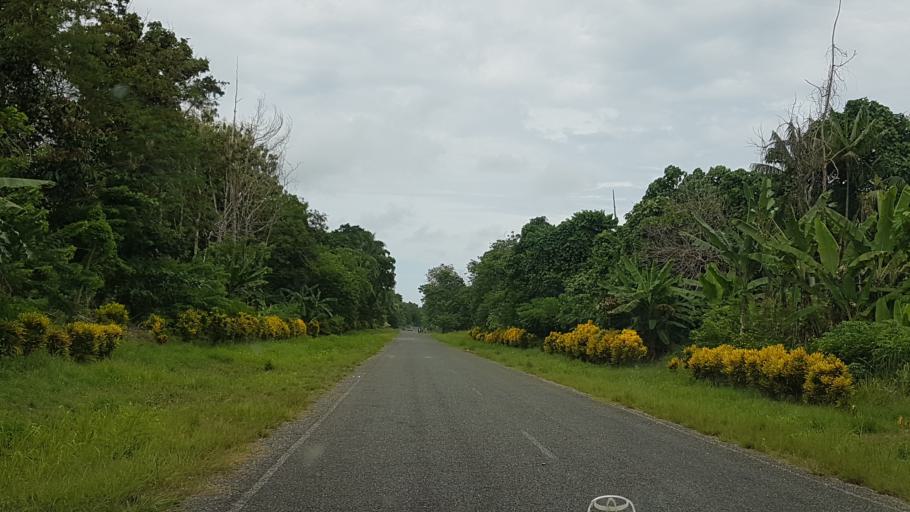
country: PG
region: Madang
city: Madang
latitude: -4.4428
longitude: 145.3542
